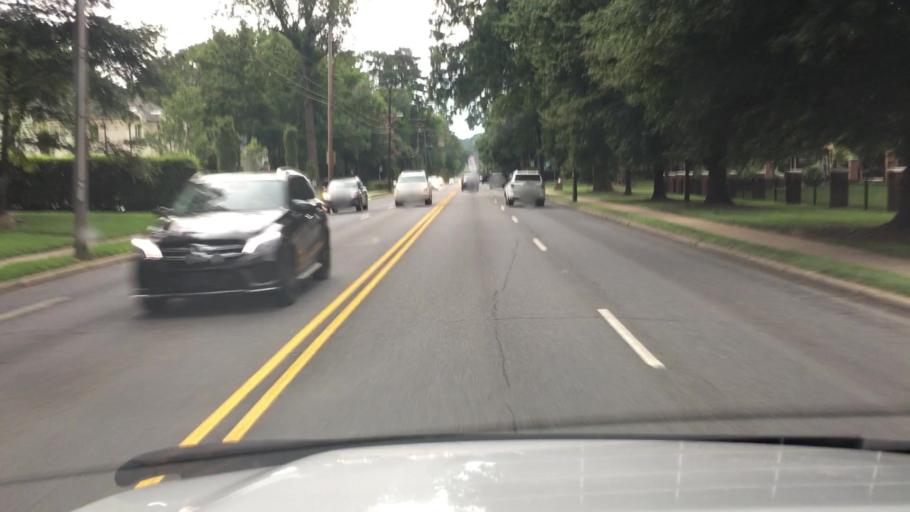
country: US
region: North Carolina
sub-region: Mecklenburg County
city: Charlotte
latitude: 35.1883
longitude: -80.8224
